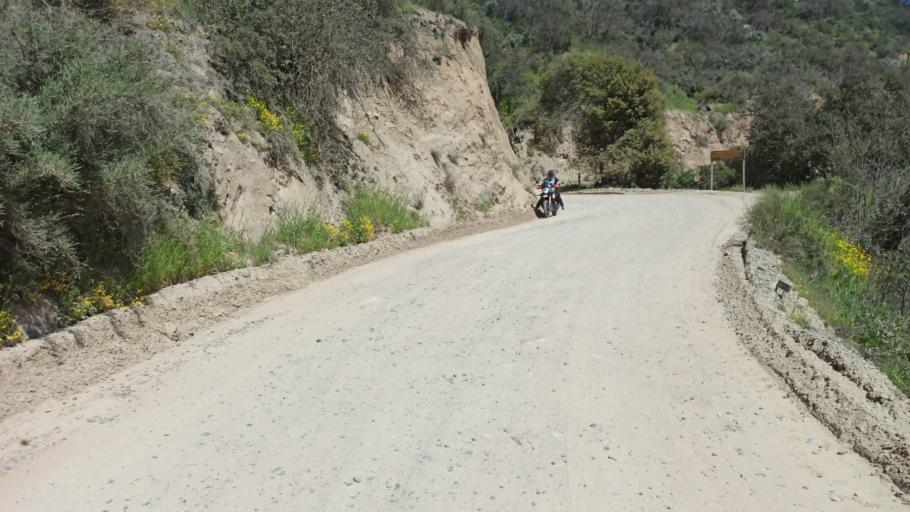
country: CL
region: Valparaiso
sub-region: Provincia de Marga Marga
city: Limache
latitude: -33.2048
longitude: -71.2570
